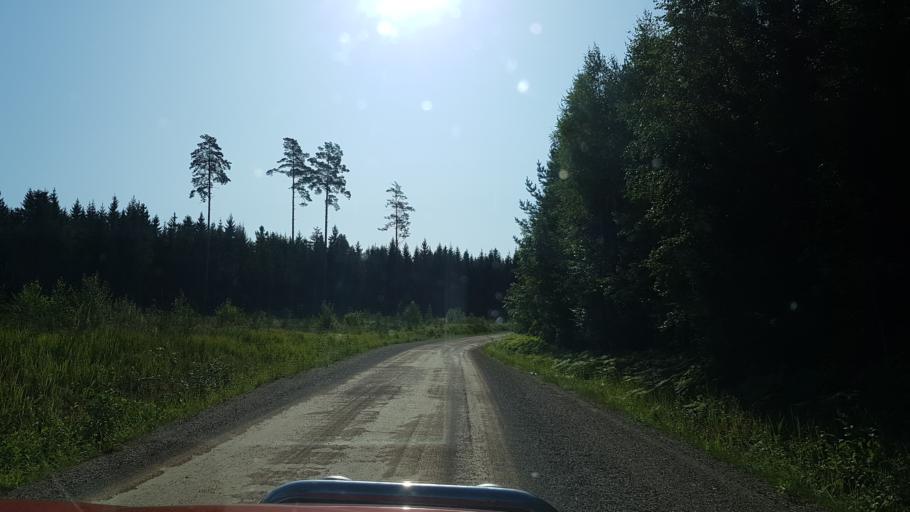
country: LV
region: Apes Novads
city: Ape
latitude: 57.6184
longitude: 26.8019
